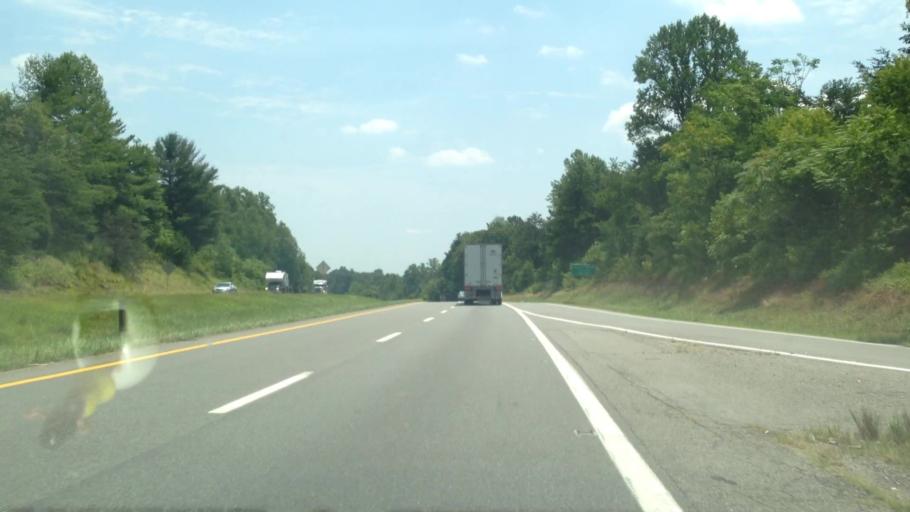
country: US
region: Virginia
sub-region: City of Martinsville
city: Martinsville
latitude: 36.6269
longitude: -79.8774
